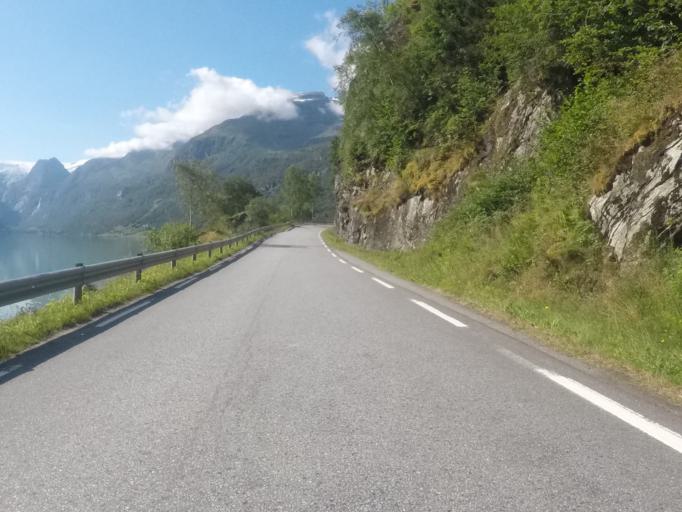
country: NO
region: Sogn og Fjordane
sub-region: Stryn
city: Stryn
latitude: 61.7541
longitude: 6.7973
